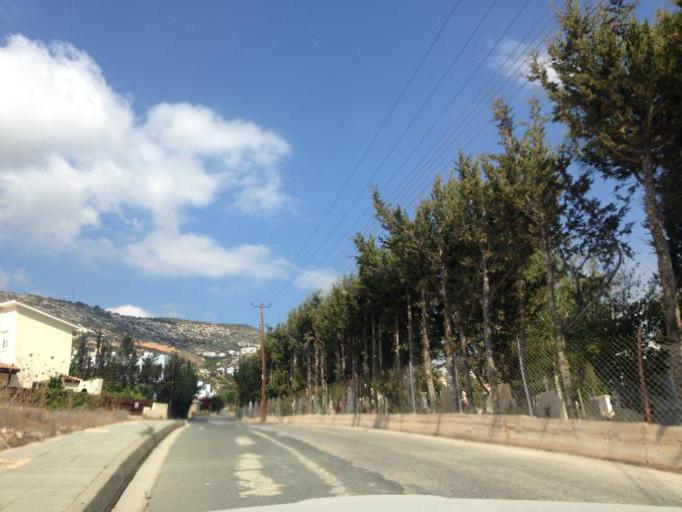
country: CY
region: Pafos
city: Pegeia
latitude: 34.8797
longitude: 32.3711
